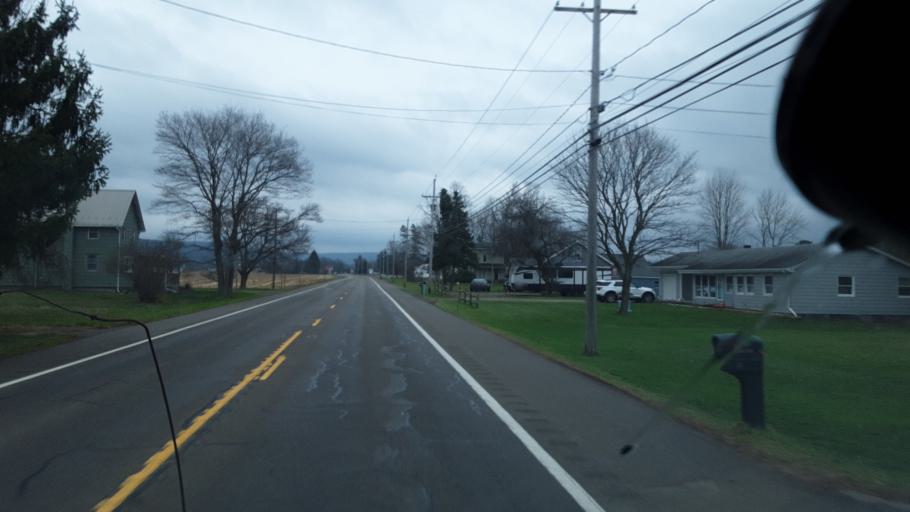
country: US
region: New York
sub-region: Allegany County
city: Belmont
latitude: 42.2082
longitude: -78.0133
